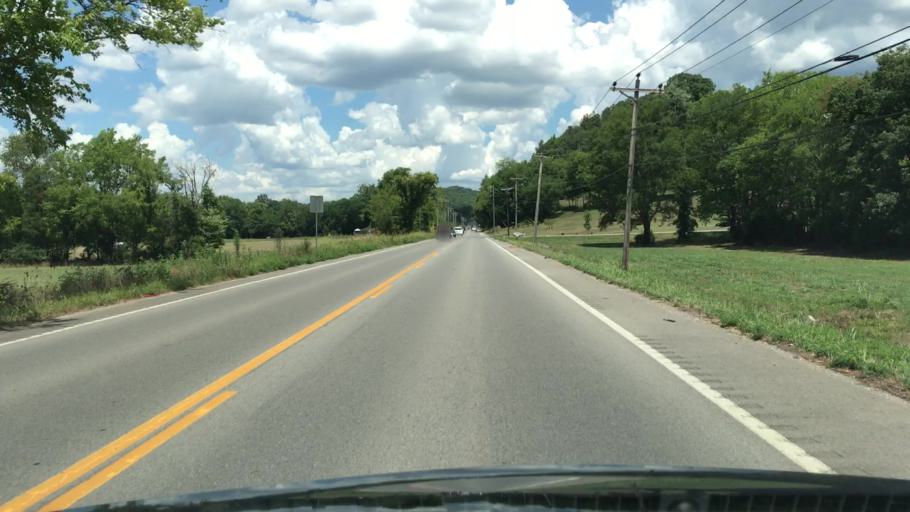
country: US
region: Tennessee
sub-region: Williamson County
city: Nolensville
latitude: 35.8848
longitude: -86.6630
